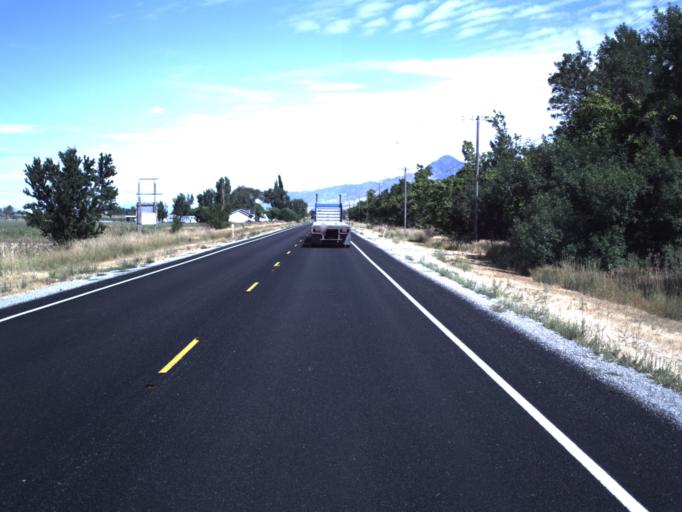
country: US
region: Utah
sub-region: Box Elder County
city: Garland
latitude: 41.7731
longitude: -112.1490
